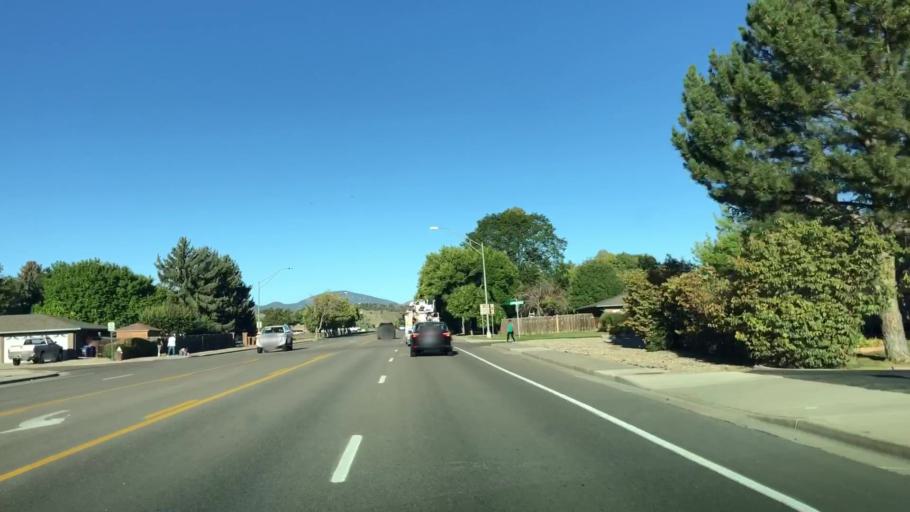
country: US
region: Colorado
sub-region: Larimer County
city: Loveland
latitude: 40.4219
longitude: -105.1122
